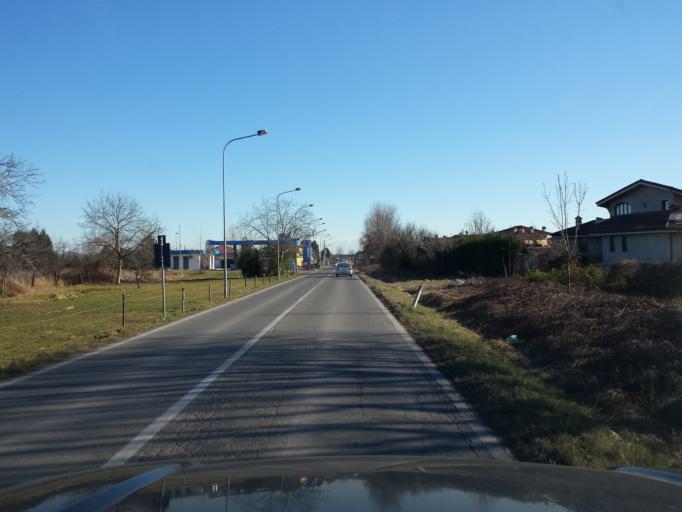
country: IT
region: Piedmont
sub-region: Provincia di Torino
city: Castellamonte
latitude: 45.3698
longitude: 7.7177
